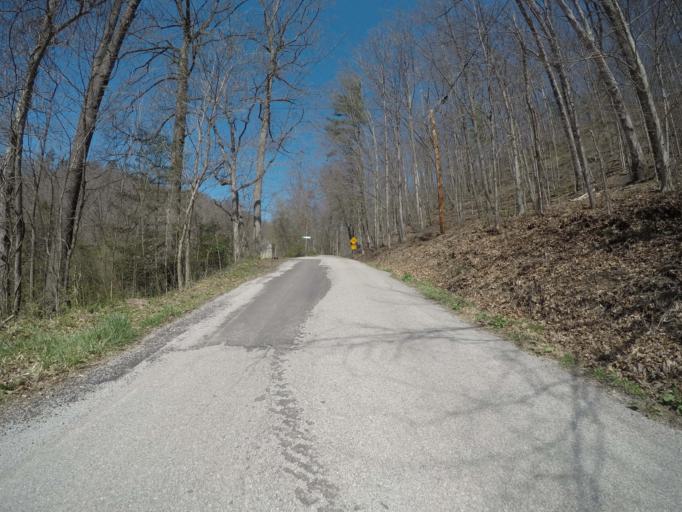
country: US
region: West Virginia
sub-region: Kanawha County
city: Charleston
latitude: 38.4089
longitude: -81.5889
